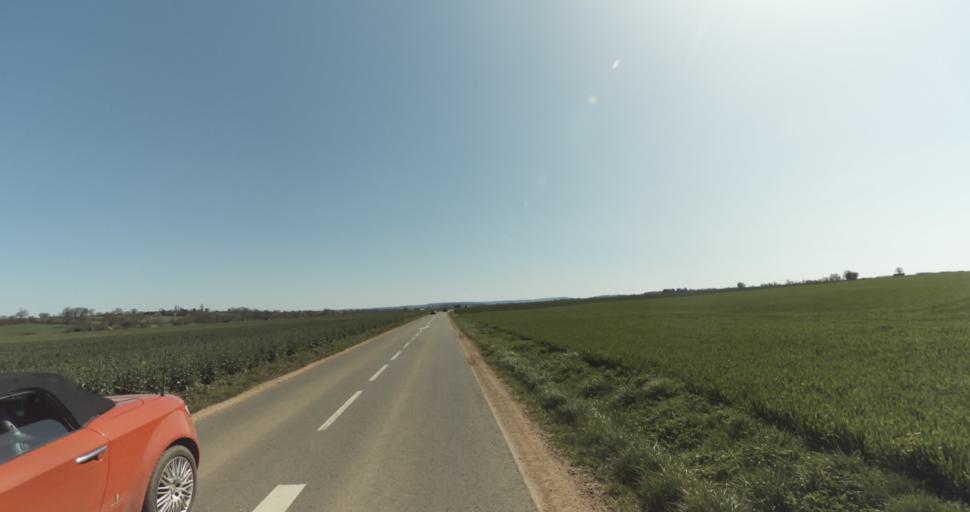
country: FR
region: Lower Normandy
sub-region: Departement du Calvados
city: Saint-Pierre-sur-Dives
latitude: 49.0113
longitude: -0.0295
